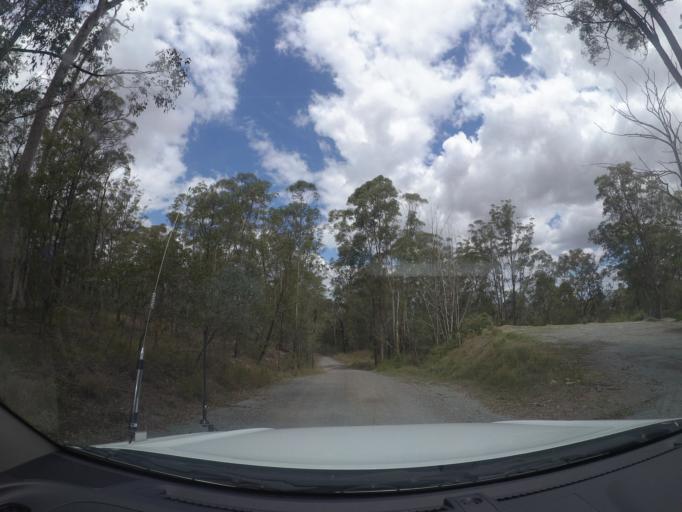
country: AU
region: Queensland
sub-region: Logan
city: Cedar Vale
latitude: -27.9028
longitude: 153.0317
